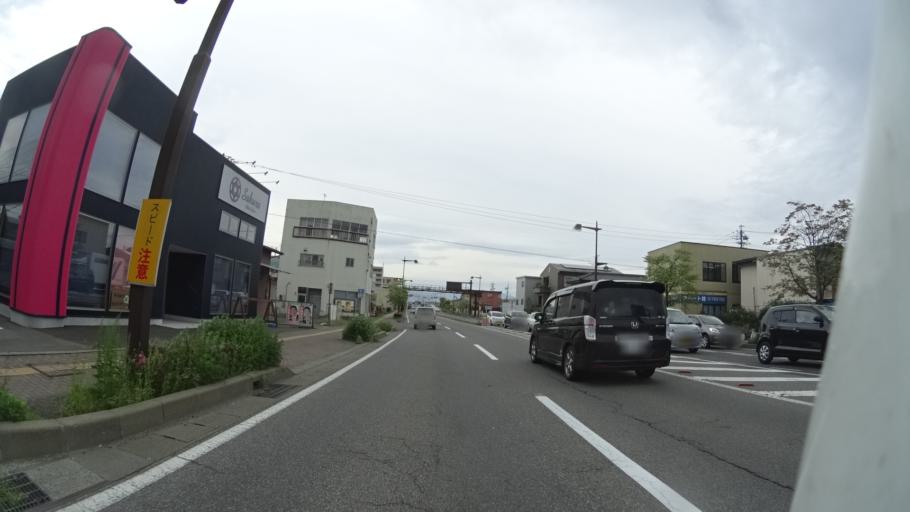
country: JP
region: Nagano
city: Nagano-shi
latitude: 36.6183
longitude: 138.1815
